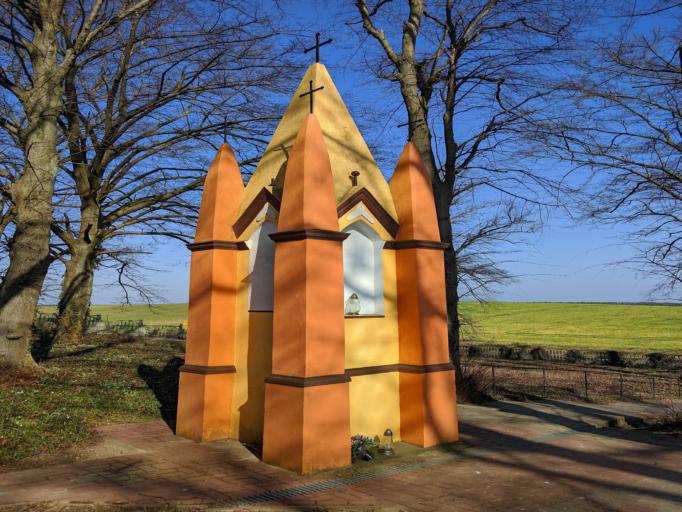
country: PL
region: Lubusz
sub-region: Powiat miedzyrzecki
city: Bledzew
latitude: 52.5059
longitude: 15.3397
